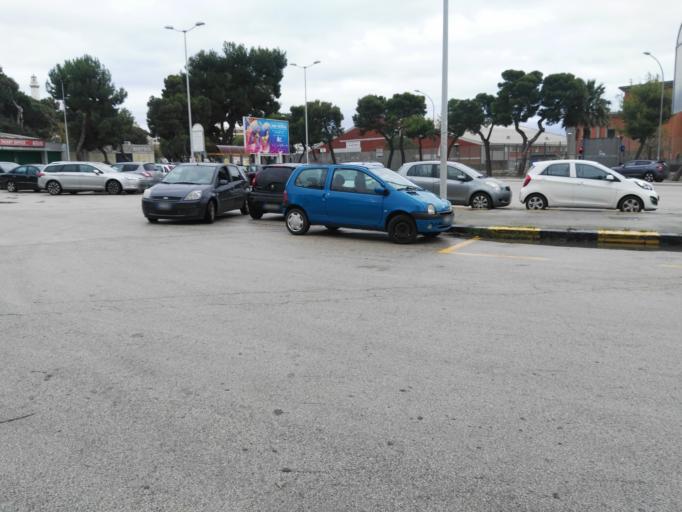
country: IT
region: Apulia
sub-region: Provincia di Bari
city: Bari
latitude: 41.1348
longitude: 16.8438
